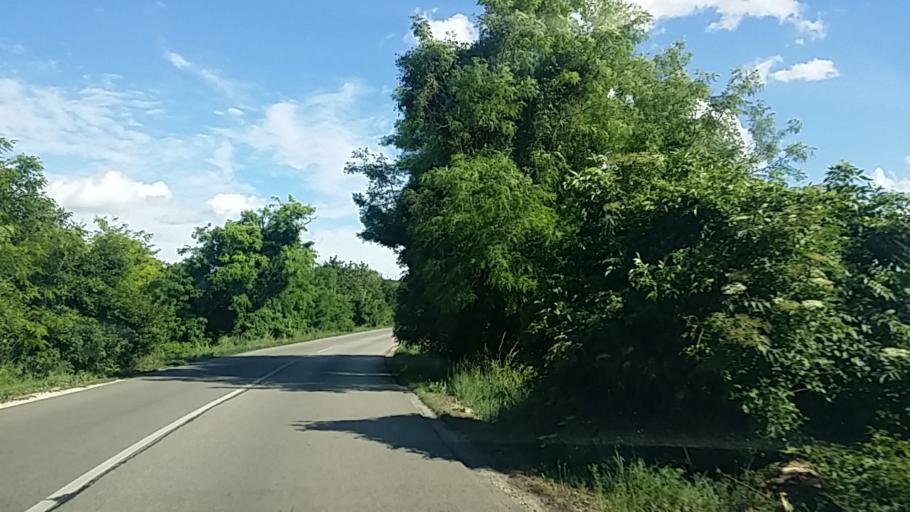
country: HU
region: Pest
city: Zsambek
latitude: 47.5655
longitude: 18.6908
